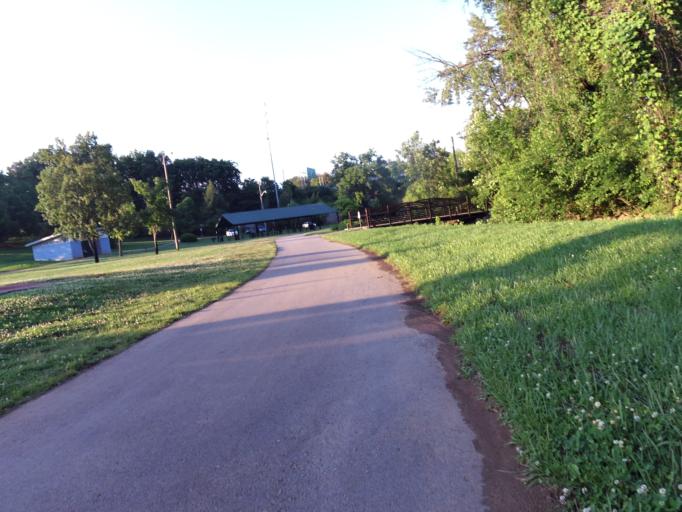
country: US
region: Tennessee
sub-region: Knox County
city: Knoxville
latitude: 35.9536
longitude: -83.9456
